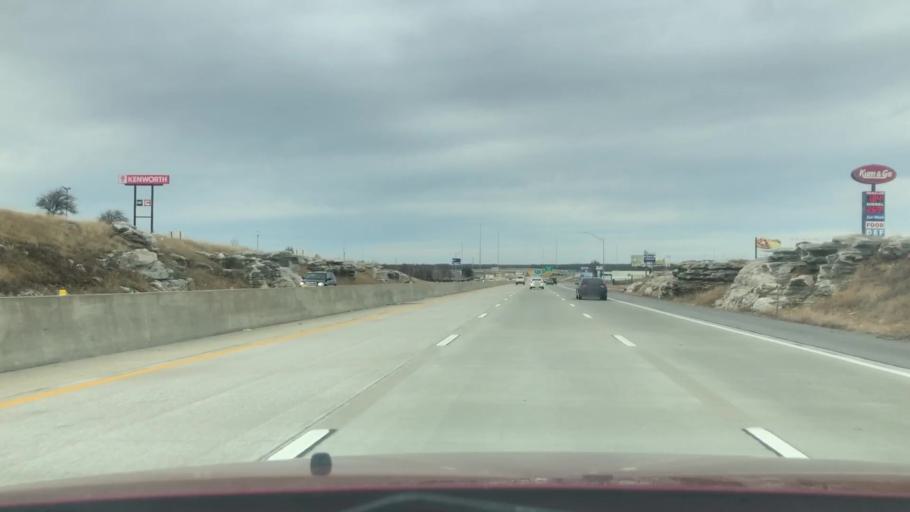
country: US
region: Missouri
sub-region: Greene County
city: Springfield
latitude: 37.2393
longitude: -93.2246
